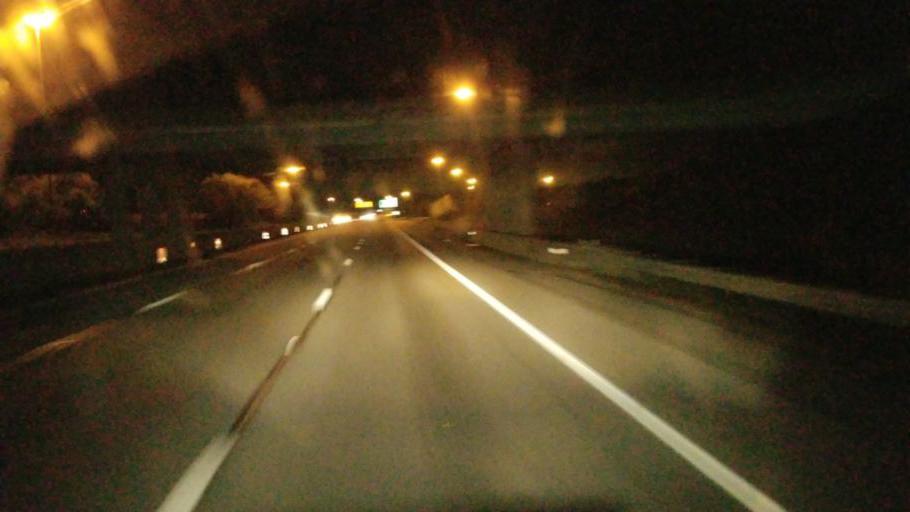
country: US
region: Ohio
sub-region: Licking County
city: Buckeye Lake
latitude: 39.9461
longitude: -82.4709
